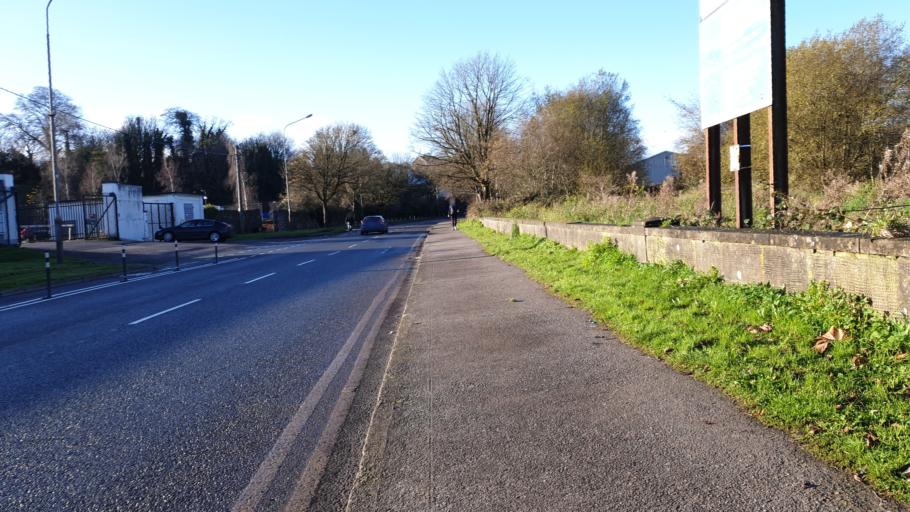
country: IE
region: Munster
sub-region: County Cork
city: Cork
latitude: 51.8962
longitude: -8.4449
